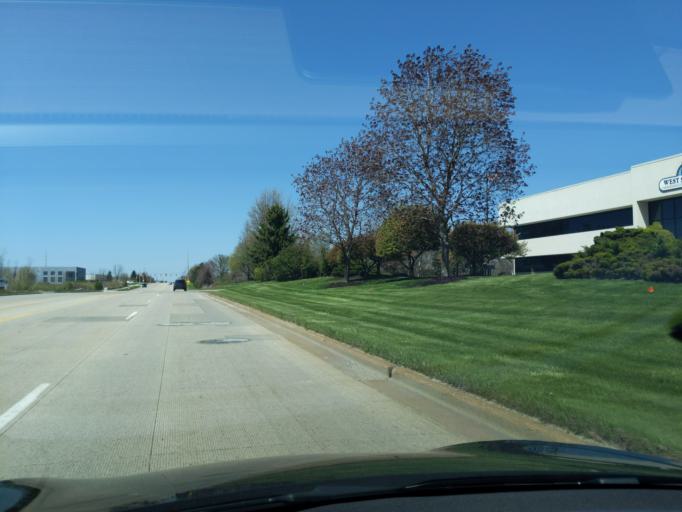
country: US
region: Michigan
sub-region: Kent County
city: Caledonia
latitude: 42.8653
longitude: -85.5462
